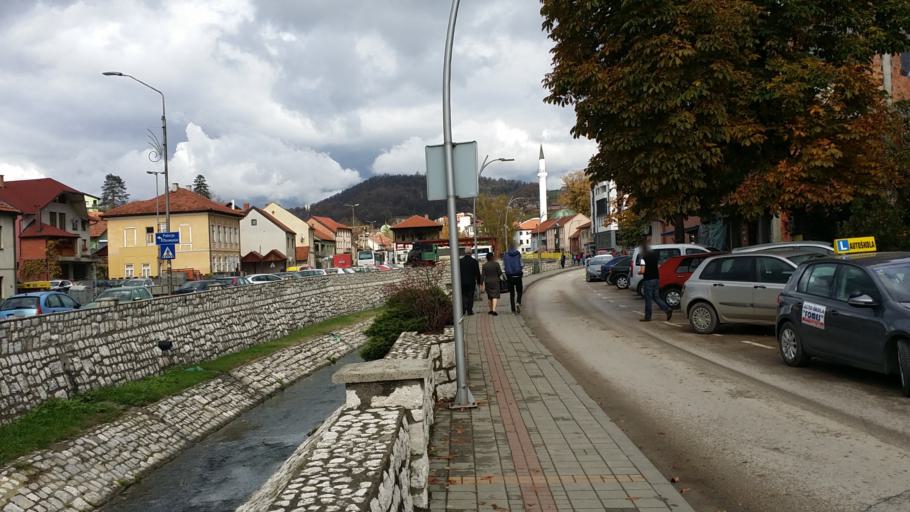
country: BA
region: Federation of Bosnia and Herzegovina
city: Gracanica
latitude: 44.7030
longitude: 18.3087
